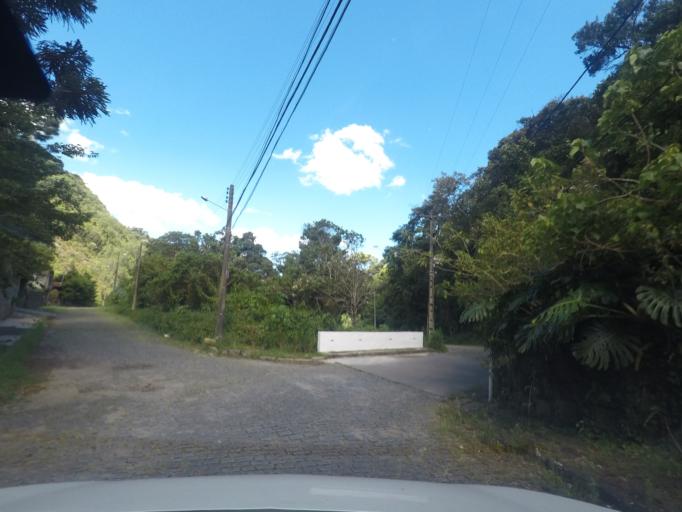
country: BR
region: Rio de Janeiro
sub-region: Teresopolis
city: Teresopolis
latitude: -22.4333
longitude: -42.9936
